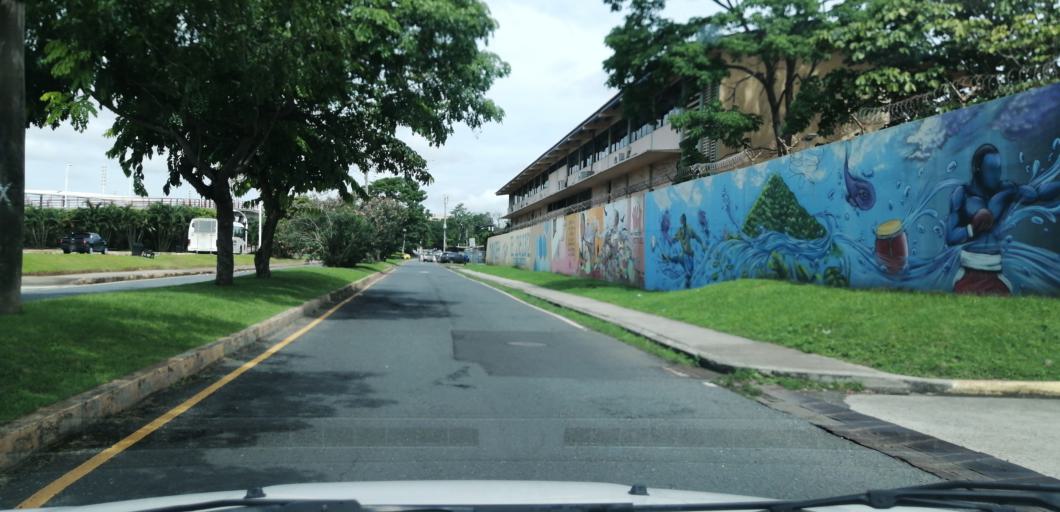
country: PA
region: Panama
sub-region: Distrito de Panama
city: Ancon
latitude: 8.9477
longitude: -79.5471
